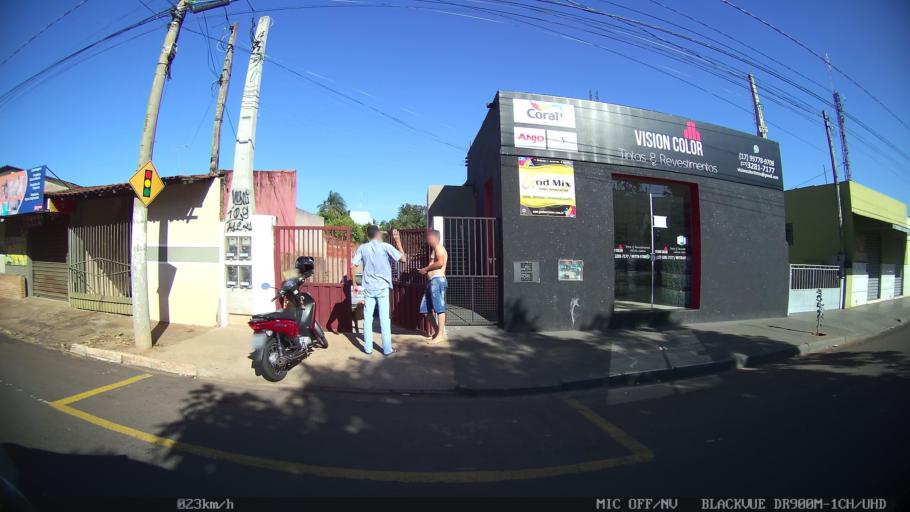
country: BR
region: Sao Paulo
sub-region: Olimpia
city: Olimpia
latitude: -20.7396
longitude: -48.9042
